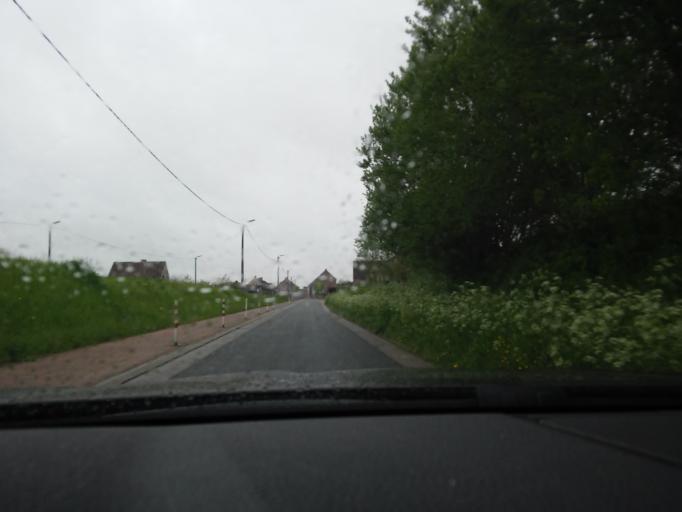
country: BE
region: Flanders
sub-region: Provincie Vlaams-Brabant
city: Pepingen
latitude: 50.7630
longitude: 4.1644
